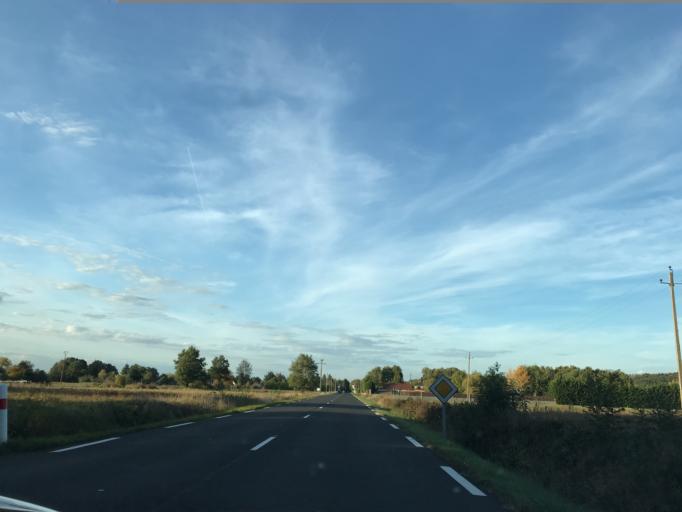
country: FR
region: Auvergne
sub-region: Departement du Puy-de-Dome
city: Puy-Guillaume
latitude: 45.9937
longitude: 3.4859
